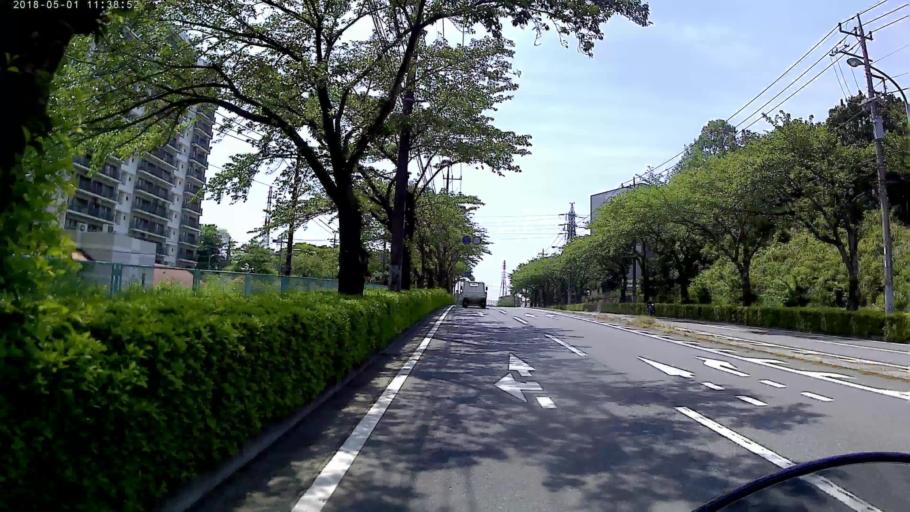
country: JP
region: Kanagawa
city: Minami-rinkan
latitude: 35.5064
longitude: 139.4902
